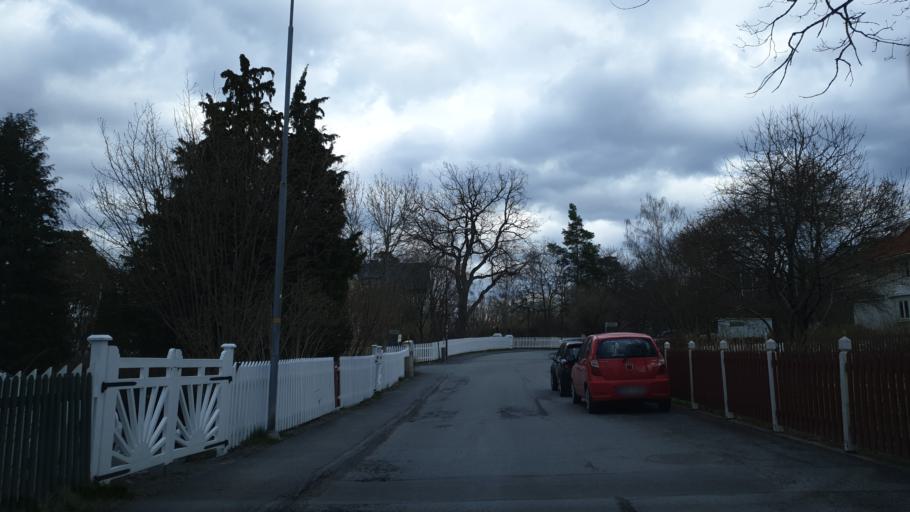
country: SE
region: Stockholm
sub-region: Nacka Kommun
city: Saltsjobaden
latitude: 59.2799
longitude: 18.3023
